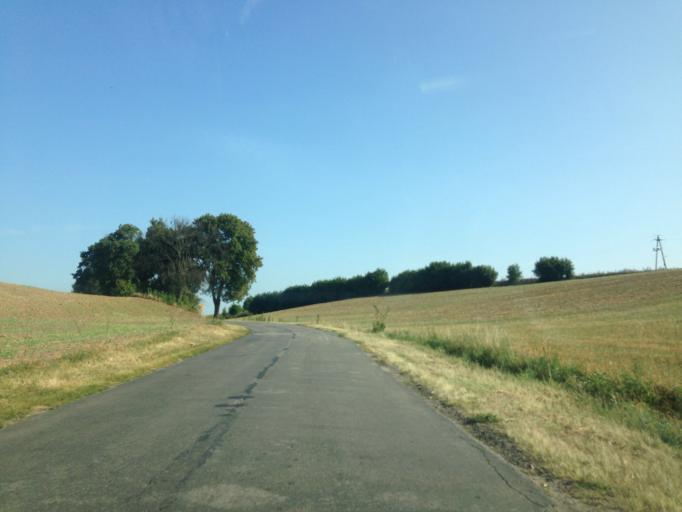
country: PL
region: Kujawsko-Pomorskie
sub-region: Powiat brodnicki
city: Brzozie
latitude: 53.3144
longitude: 19.6061
